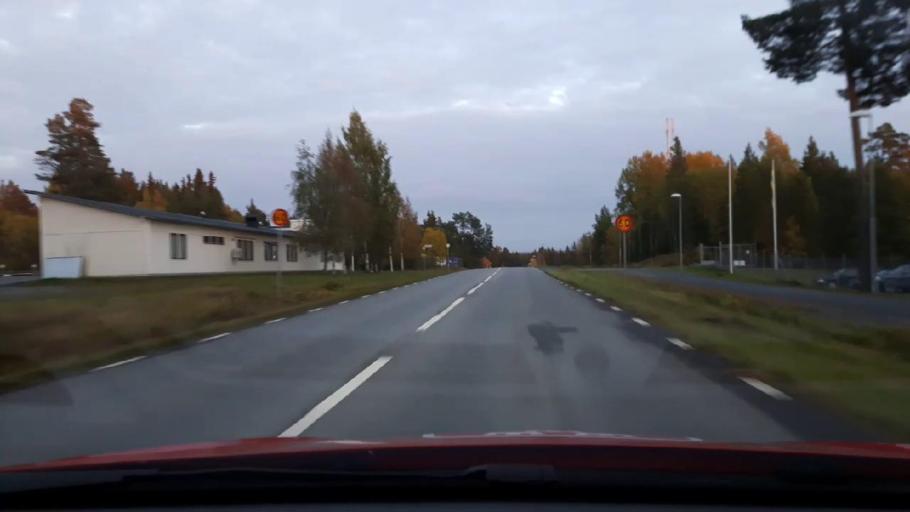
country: SE
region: Jaemtland
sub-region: OEstersunds Kommun
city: Ostersund
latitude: 63.2168
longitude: 14.6139
